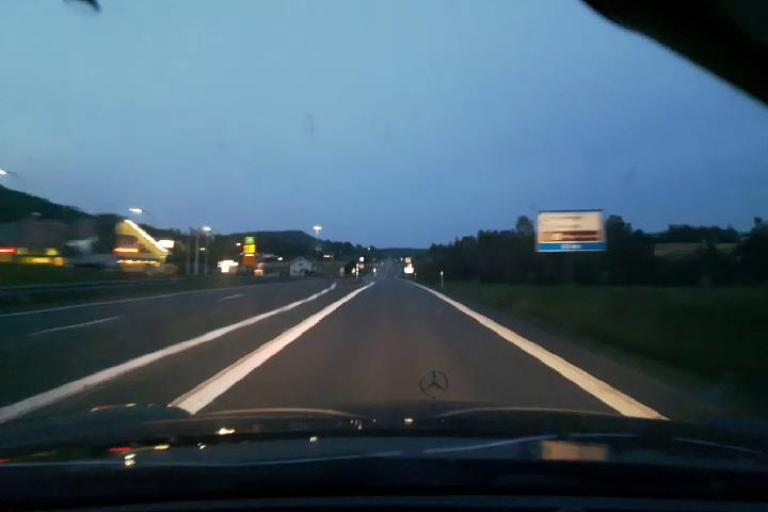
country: SE
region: Vaesternorrland
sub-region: Kramfors Kommun
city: Nordingra
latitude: 63.0576
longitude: 18.3402
